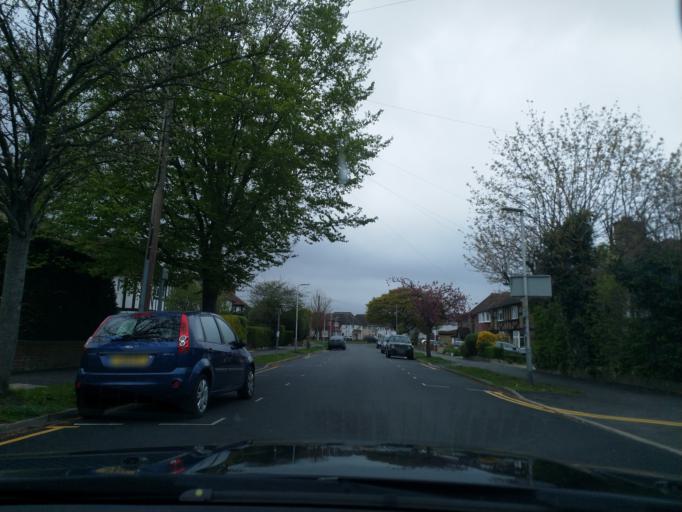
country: GB
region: England
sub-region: Greater London
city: Northolt
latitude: 51.5616
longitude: -0.3934
